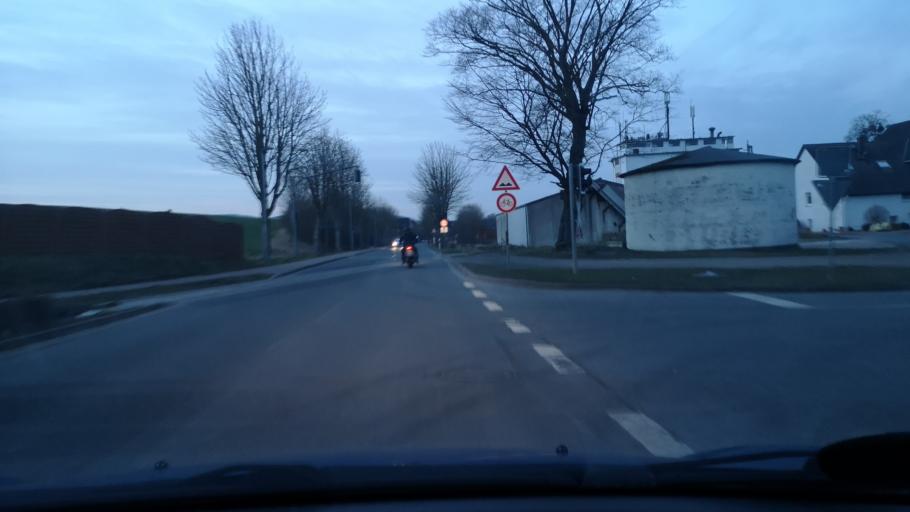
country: DE
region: Lower Saxony
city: Salzhemmendorf
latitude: 52.0625
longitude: 9.5868
